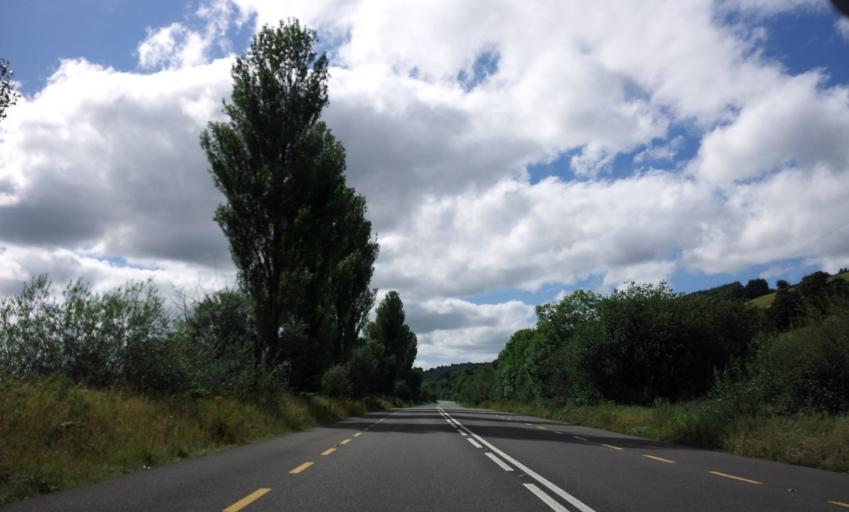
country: IE
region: Munster
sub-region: County Cork
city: Killumney
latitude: 51.8673
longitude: -8.7531
